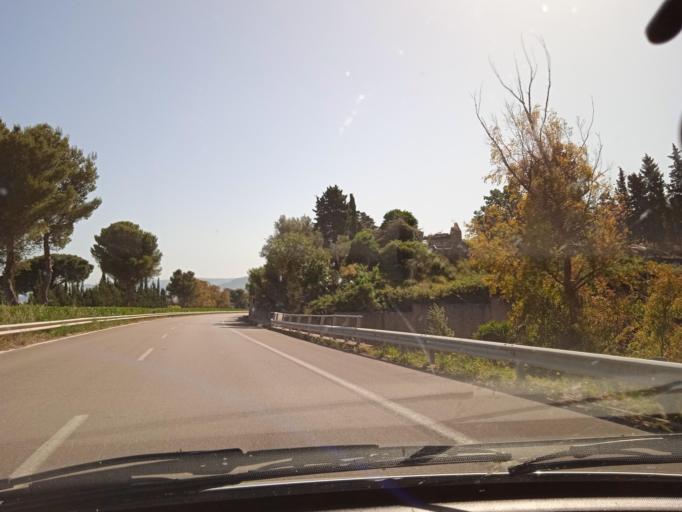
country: IT
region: Sicily
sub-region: Messina
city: Sant'Agata di Militello
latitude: 38.0614
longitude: 14.6362
